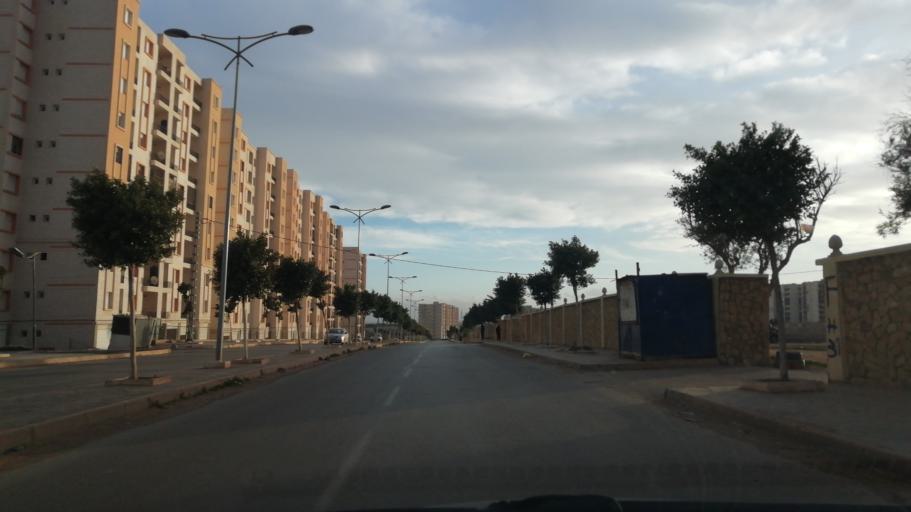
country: DZ
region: Oran
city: Bir el Djir
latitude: 35.6930
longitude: -0.5859
